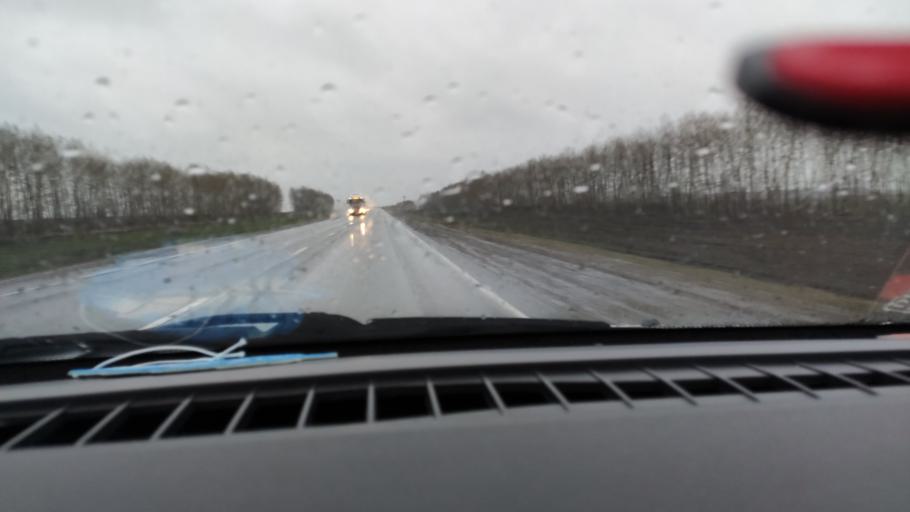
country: RU
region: Tatarstan
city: Mendeleyevsk
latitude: 55.9288
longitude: 52.2801
